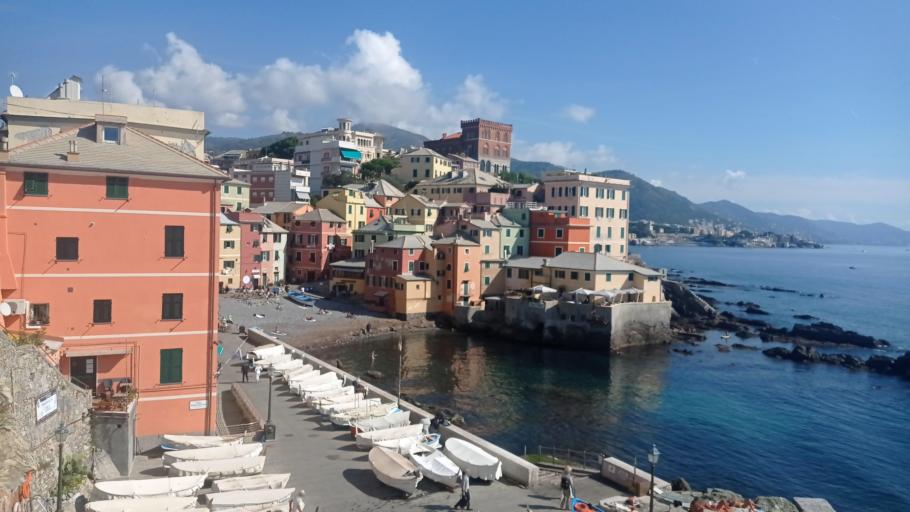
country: IT
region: Liguria
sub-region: Provincia di Genova
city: San Teodoro
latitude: 44.3897
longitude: 8.9736
